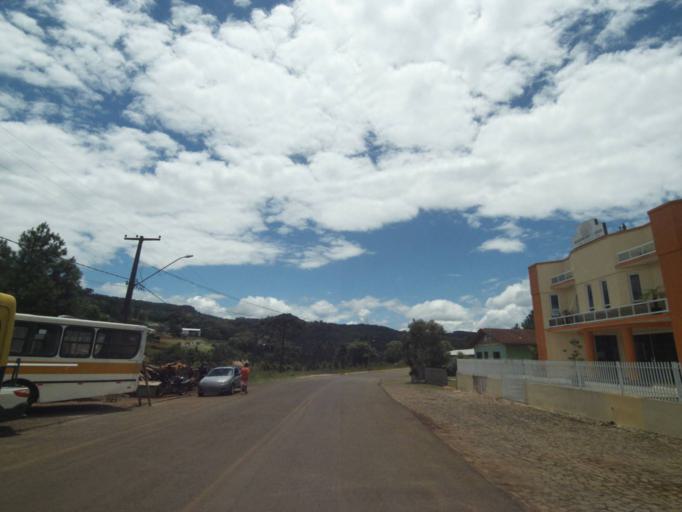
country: BR
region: Parana
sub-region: Uniao Da Vitoria
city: Uniao da Vitoria
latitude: -26.1559
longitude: -51.5518
